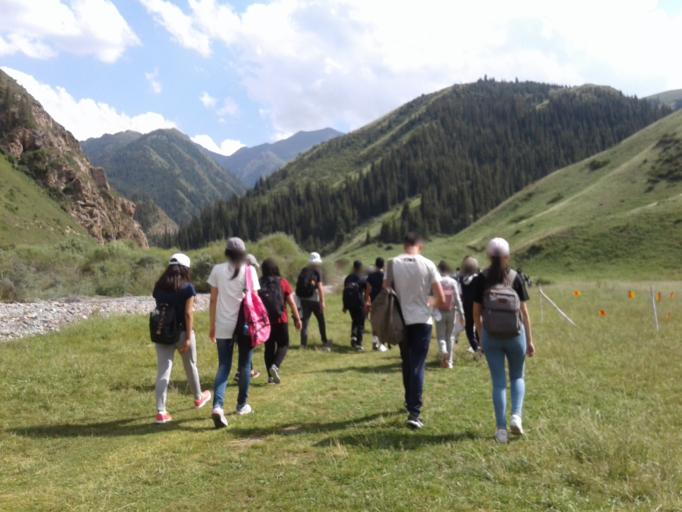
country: KG
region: Naryn
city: Naryn
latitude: 41.4593
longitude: 76.4534
